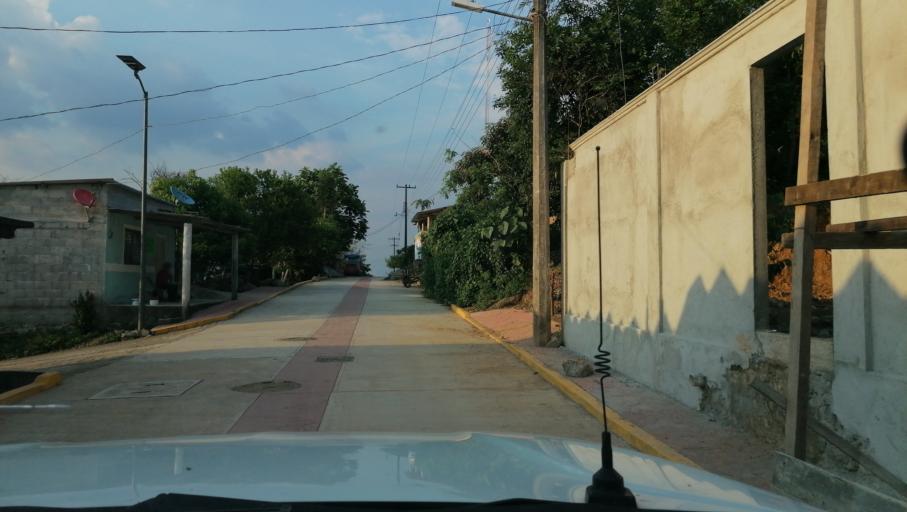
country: MX
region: Chiapas
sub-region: Juarez
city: El Triunfo 1ra. Seccion (Cardona)
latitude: 17.4906
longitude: -93.2433
